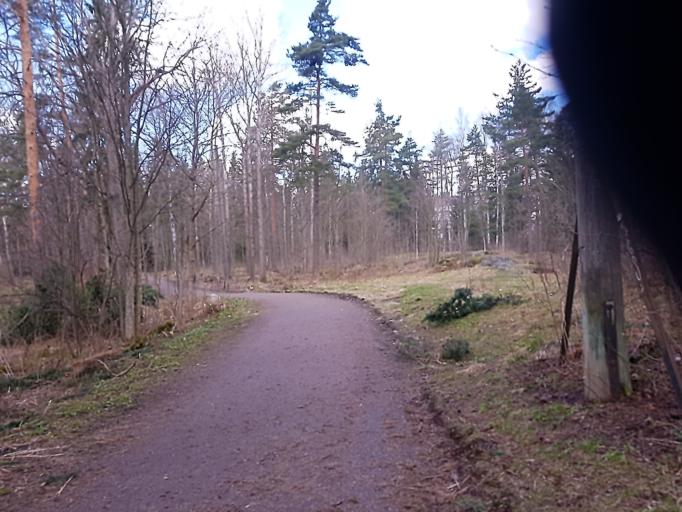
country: FI
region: Uusimaa
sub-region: Helsinki
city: Helsinki
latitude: 60.2321
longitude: 24.8969
